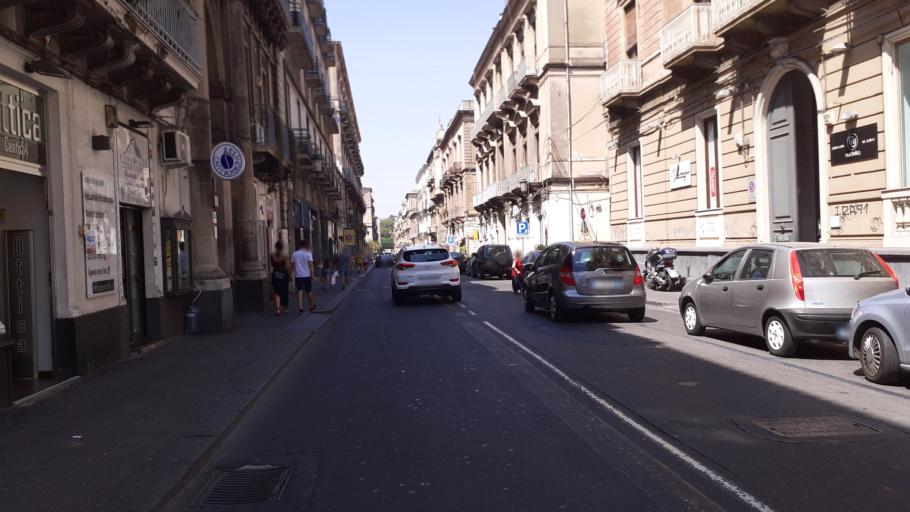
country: IT
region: Sicily
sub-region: Catania
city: Canalicchio
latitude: 37.5120
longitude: 15.0922
